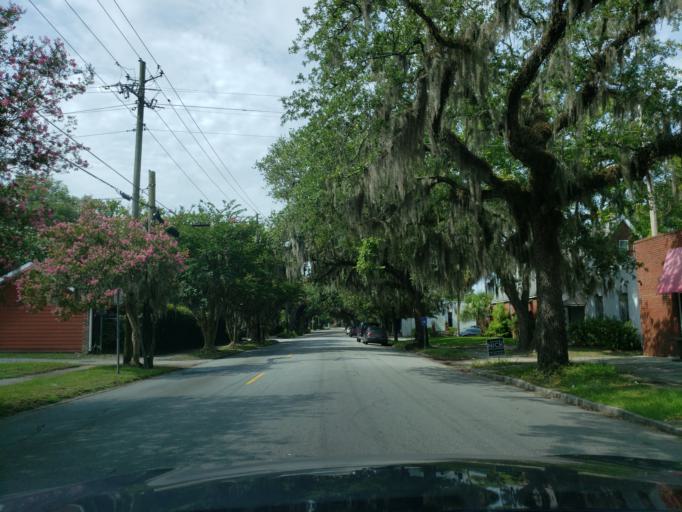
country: US
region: Georgia
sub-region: Chatham County
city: Thunderbolt
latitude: 32.0435
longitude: -81.0870
